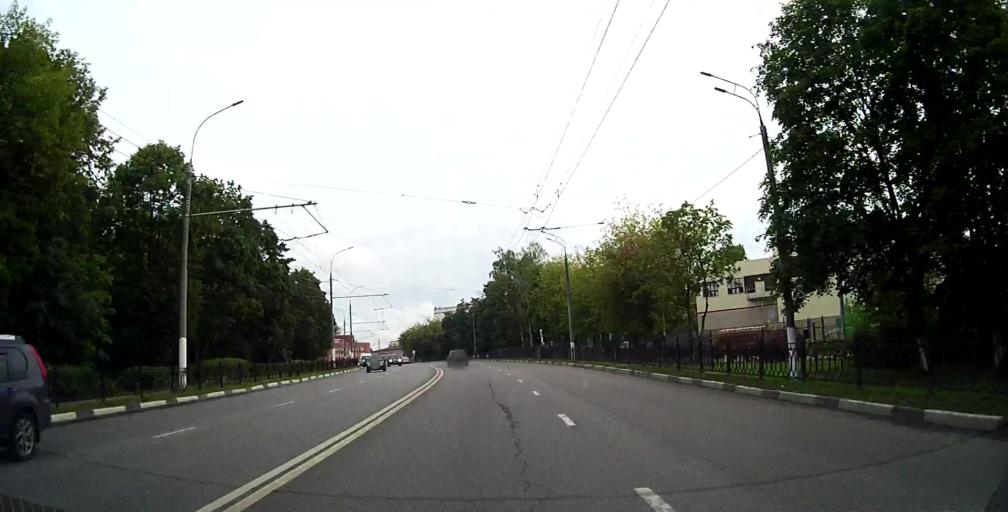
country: RU
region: Moskovskaya
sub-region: Podol'skiy Rayon
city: Podol'sk
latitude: 55.4225
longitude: 37.5665
